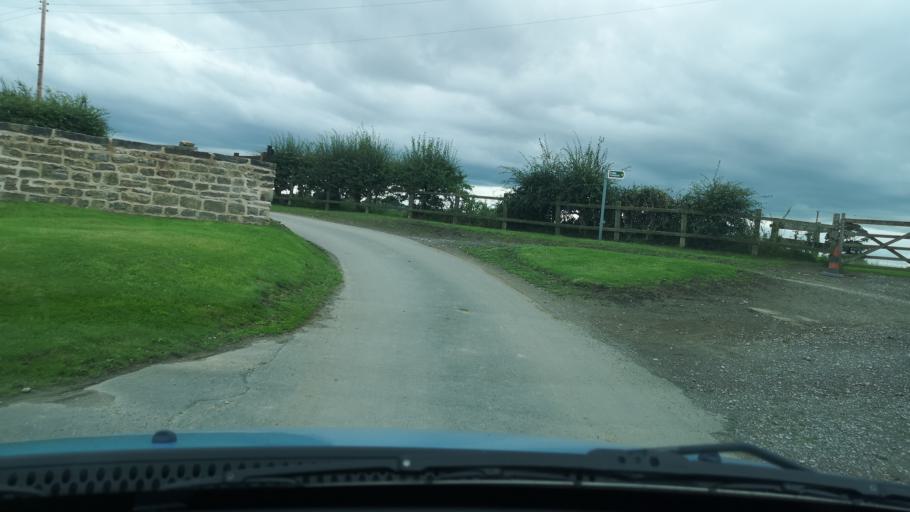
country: GB
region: England
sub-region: City and Borough of Wakefield
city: Low Ackworth
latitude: 53.6535
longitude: -1.3478
